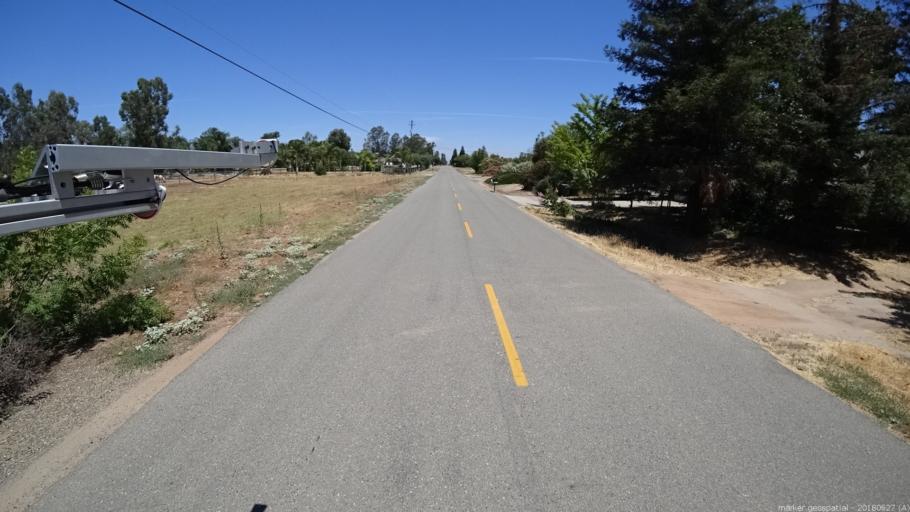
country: US
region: California
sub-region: Madera County
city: Bonadelle Ranchos-Madera Ranchos
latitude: 36.9266
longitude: -119.8645
